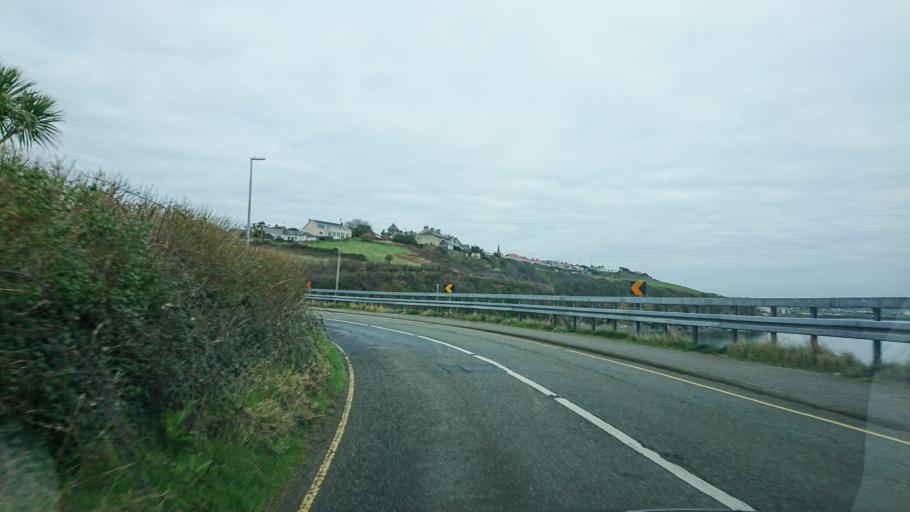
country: IE
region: Munster
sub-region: Waterford
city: Tra Mhor
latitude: 52.1528
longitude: -7.1598
